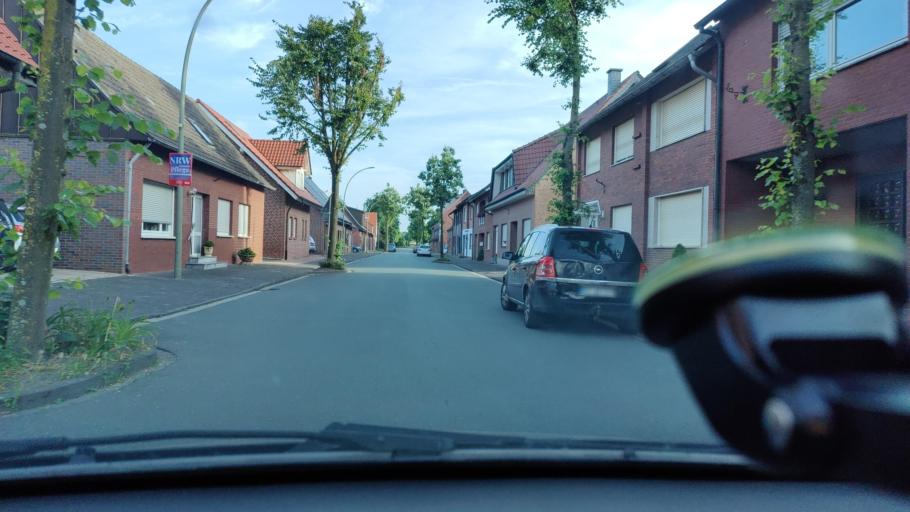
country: DE
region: North Rhine-Westphalia
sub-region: Regierungsbezirk Munster
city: Coesfeld
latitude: 52.0158
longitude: 7.2096
